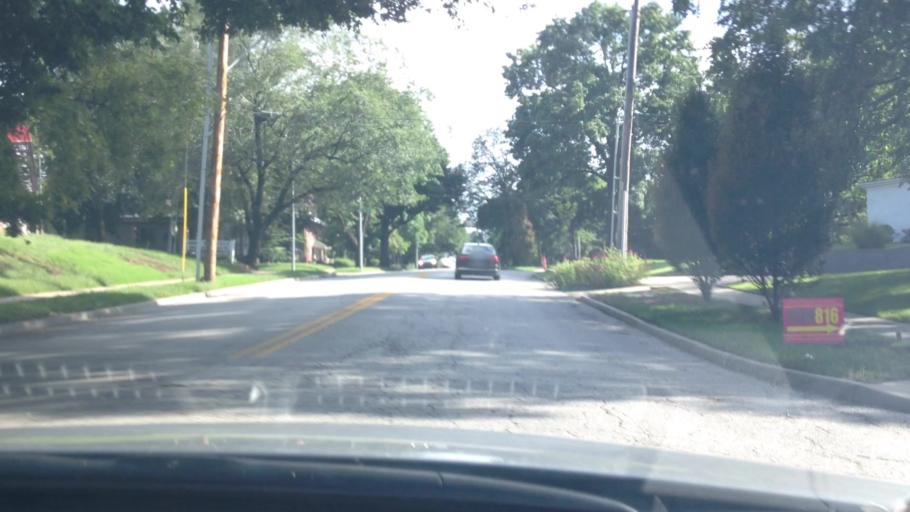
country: US
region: Kansas
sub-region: Johnson County
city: Mission Hills
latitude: 39.0172
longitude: -94.5931
